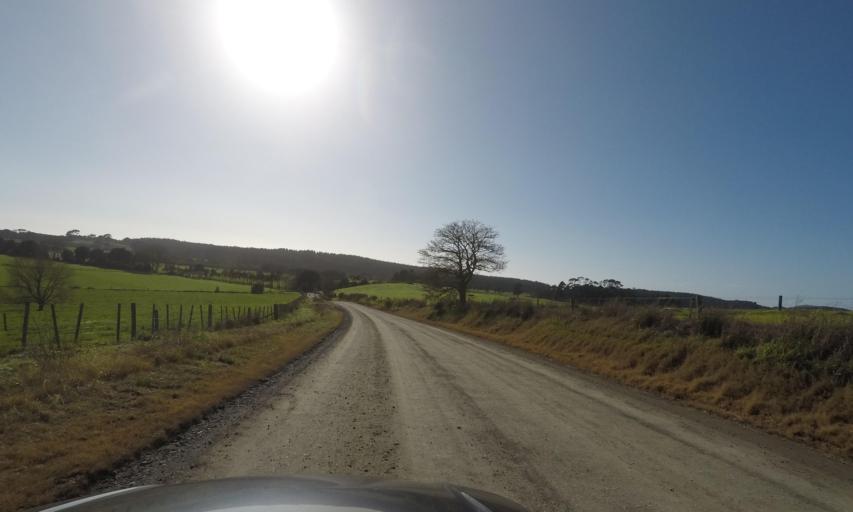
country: NZ
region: Auckland
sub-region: Auckland
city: Wellsford
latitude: -36.1596
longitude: 174.6113
